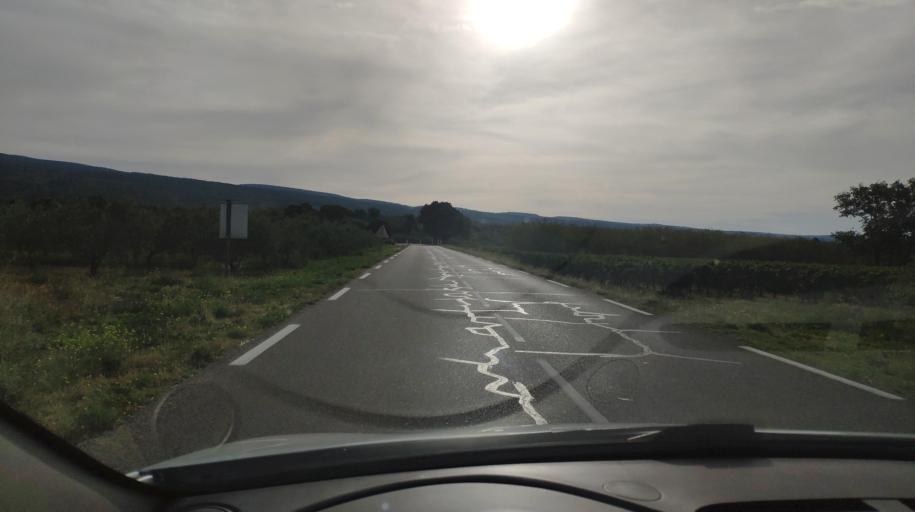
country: FR
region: Provence-Alpes-Cote d'Azur
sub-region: Departement du Vaucluse
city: Bedoin
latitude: 44.1210
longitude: 5.2065
